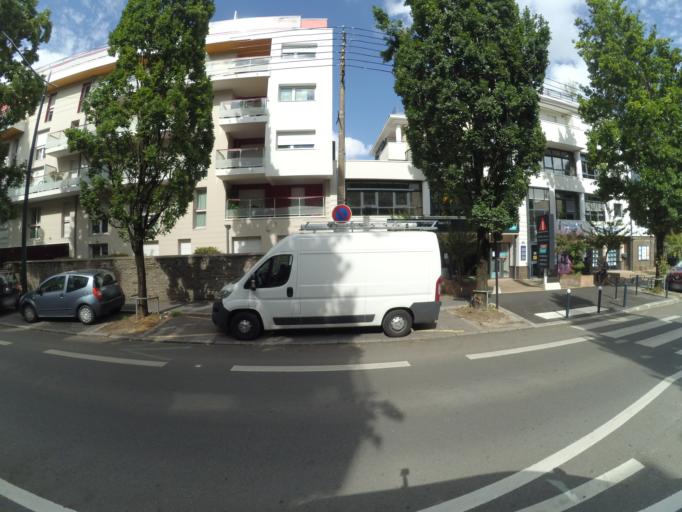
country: FR
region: Pays de la Loire
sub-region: Departement de la Loire-Atlantique
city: Nantes
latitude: 47.2391
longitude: -1.5710
